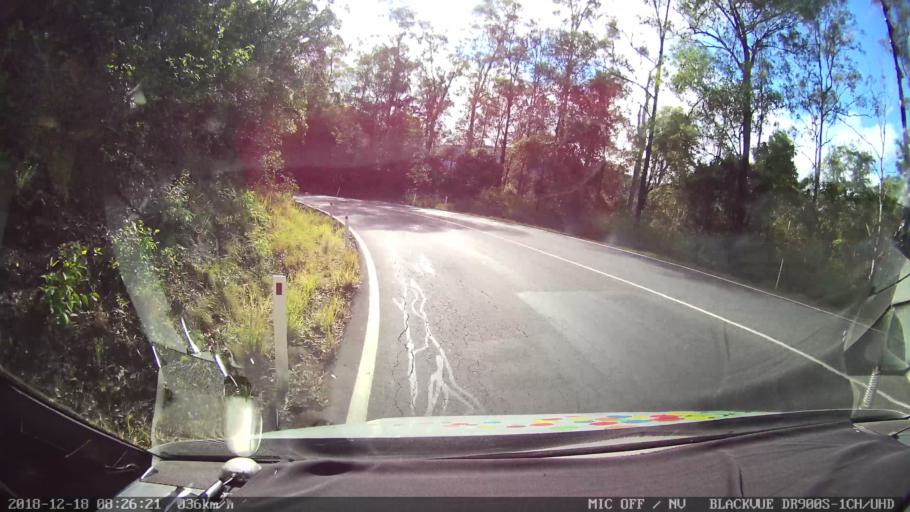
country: AU
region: New South Wales
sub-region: Kyogle
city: Kyogle
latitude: -28.3266
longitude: 152.7422
